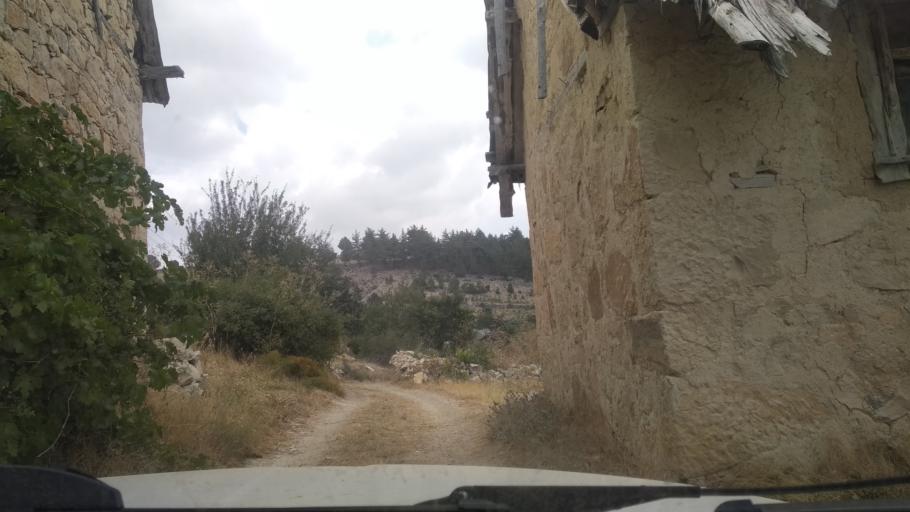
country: TR
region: Mersin
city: Sarikavak
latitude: 36.5987
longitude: 33.7277
